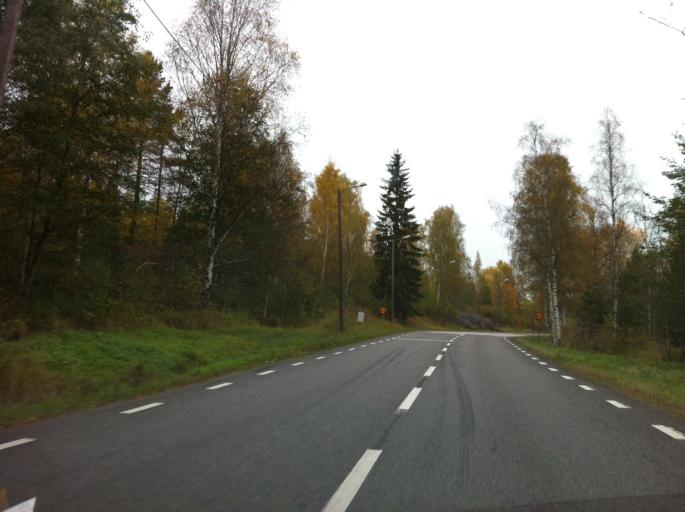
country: SE
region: Dalarna
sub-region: Ludvika Kommun
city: Grangesberg
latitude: 60.0635
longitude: 14.9859
